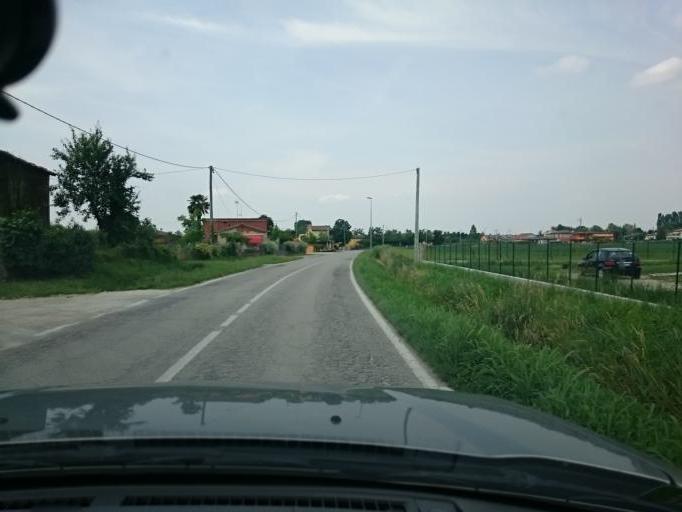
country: IT
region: Veneto
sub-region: Provincia di Padova
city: Brugine
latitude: 45.3214
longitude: 11.9836
